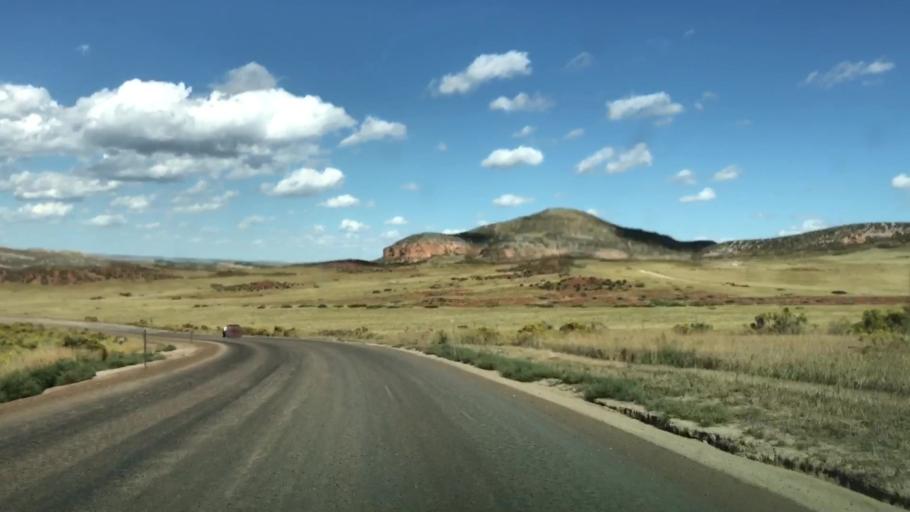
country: US
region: Colorado
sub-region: Larimer County
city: Laporte
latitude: 40.7652
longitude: -105.1679
